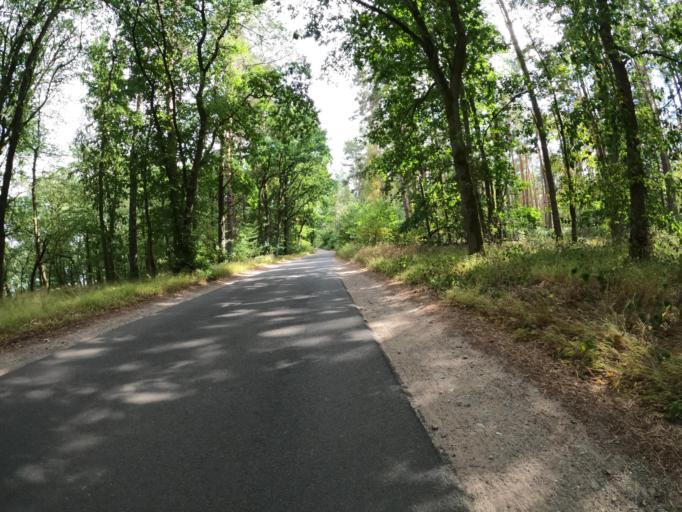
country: DE
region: Brandenburg
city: Lychen
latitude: 53.2868
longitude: 13.4282
